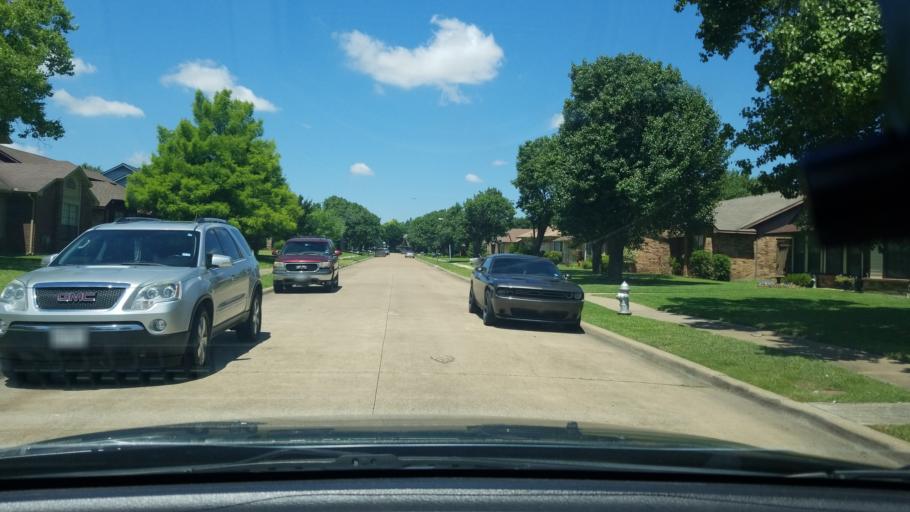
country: US
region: Texas
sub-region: Dallas County
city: Mesquite
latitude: 32.7962
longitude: -96.5991
